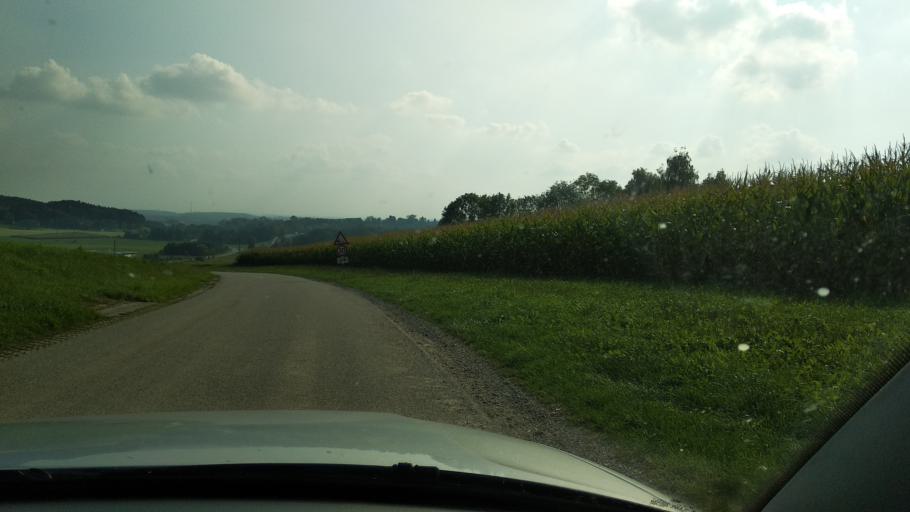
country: DE
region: Bavaria
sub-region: Upper Bavaria
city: Ebersberg
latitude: 48.0864
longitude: 11.9869
